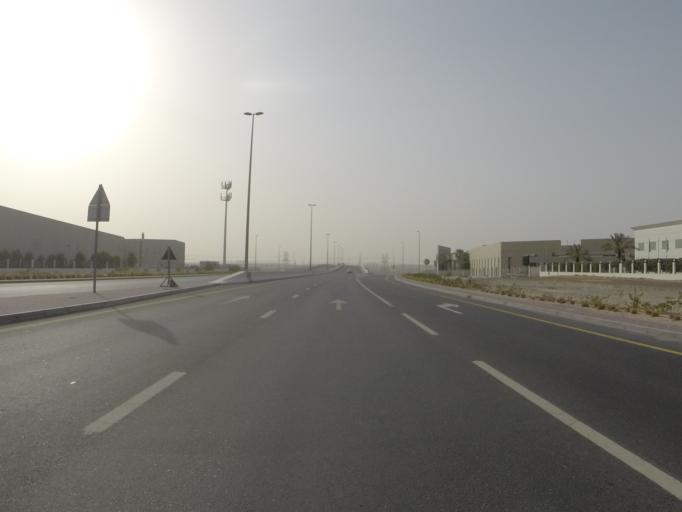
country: AE
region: Dubai
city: Dubai
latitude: 24.9599
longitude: 55.0963
